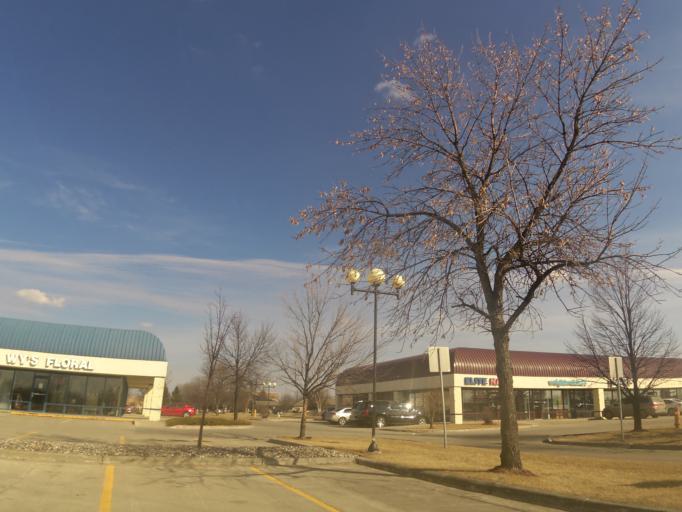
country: US
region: North Dakota
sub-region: Grand Forks County
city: Grand Forks
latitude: 47.8908
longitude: -97.0664
